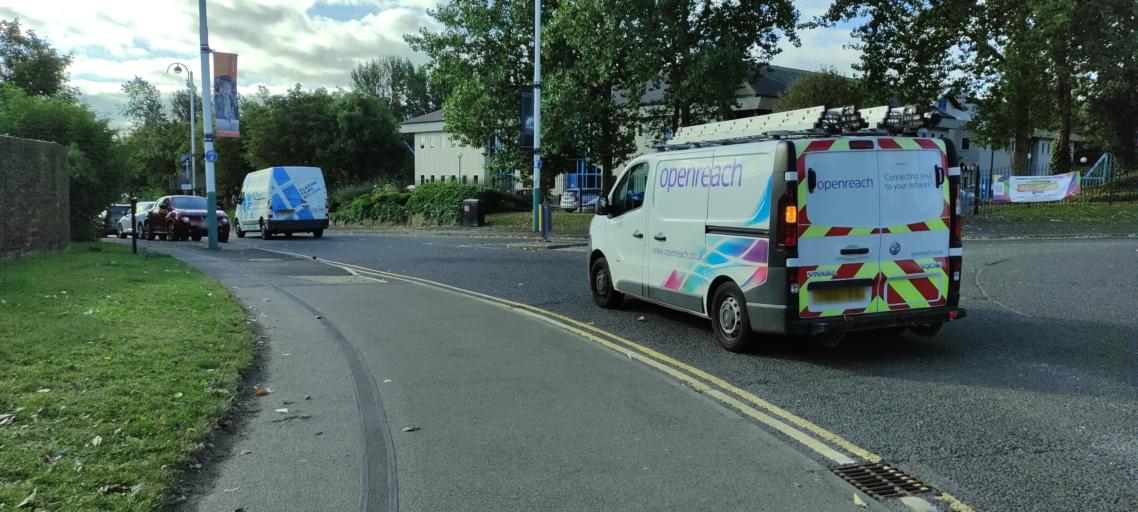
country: GB
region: England
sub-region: Sunderland
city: Sunderland
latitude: 54.9150
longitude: -1.3728
